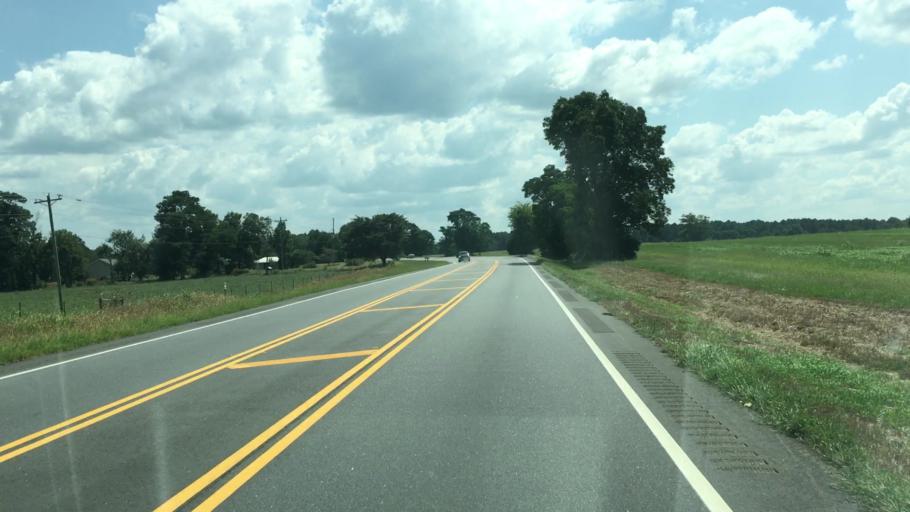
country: US
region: Georgia
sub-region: Morgan County
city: Madison
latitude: 33.5123
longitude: -83.4475
